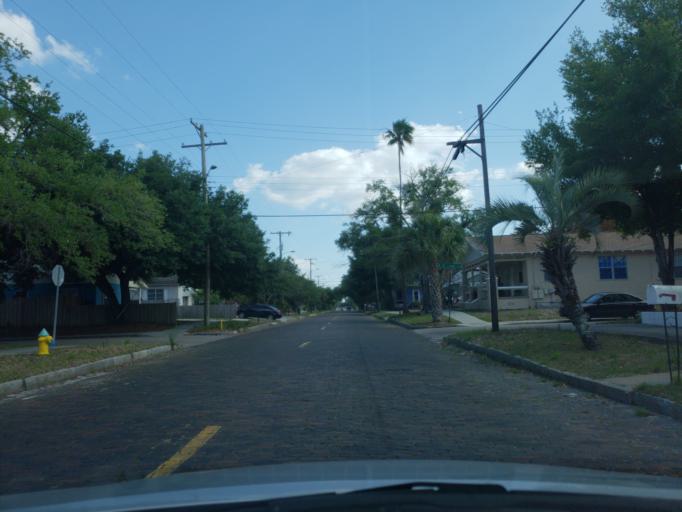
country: US
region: Florida
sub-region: Hillsborough County
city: Tampa
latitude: 27.9654
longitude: -82.4808
